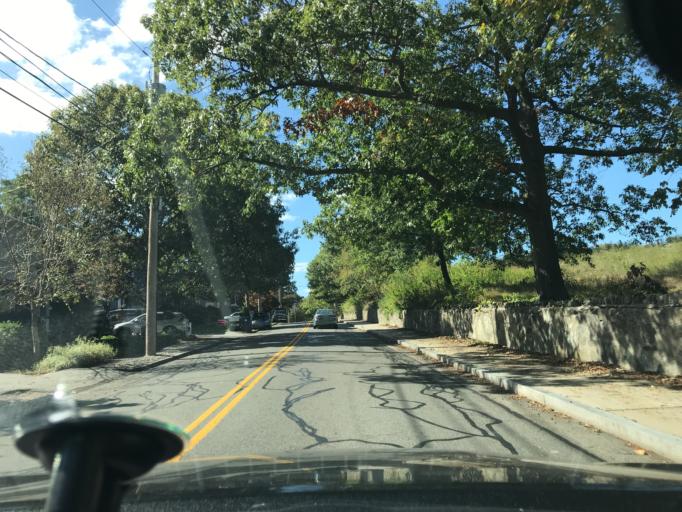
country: US
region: Massachusetts
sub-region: Suffolk County
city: Jamaica Plain
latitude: 42.2947
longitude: -71.1320
